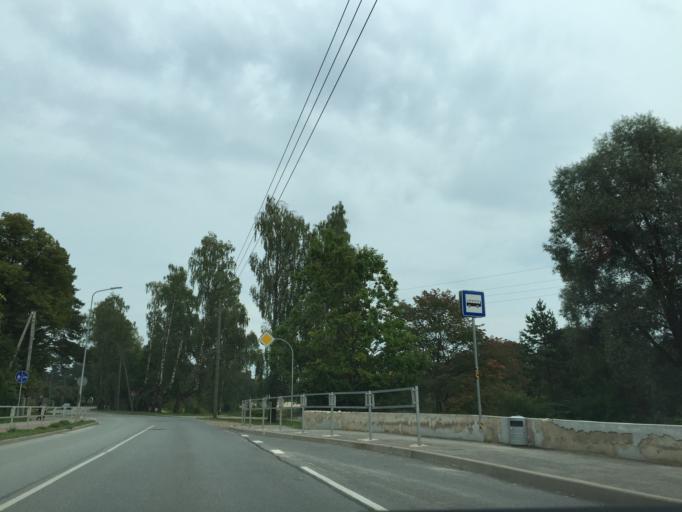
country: LV
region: Ogre
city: Ogre
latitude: 56.8154
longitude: 24.6247
